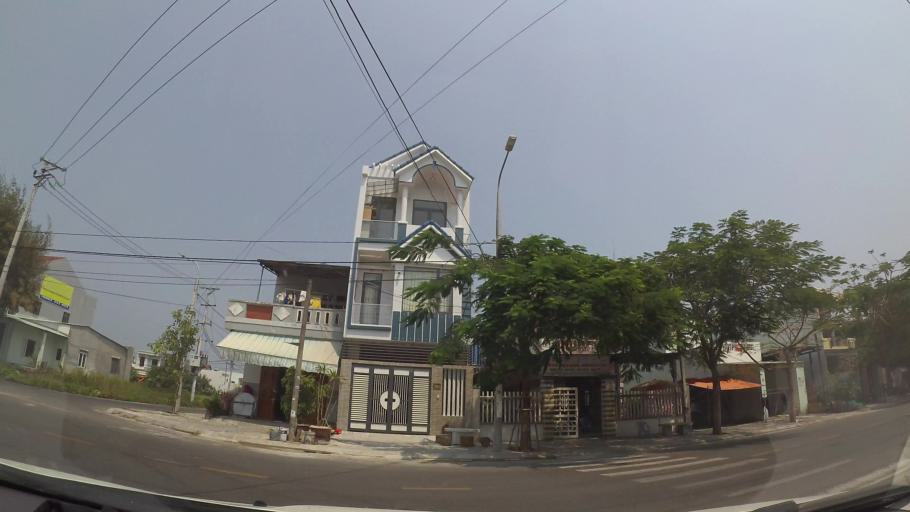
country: VN
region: Da Nang
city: Ngu Hanh Son
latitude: 15.9898
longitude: 108.2673
